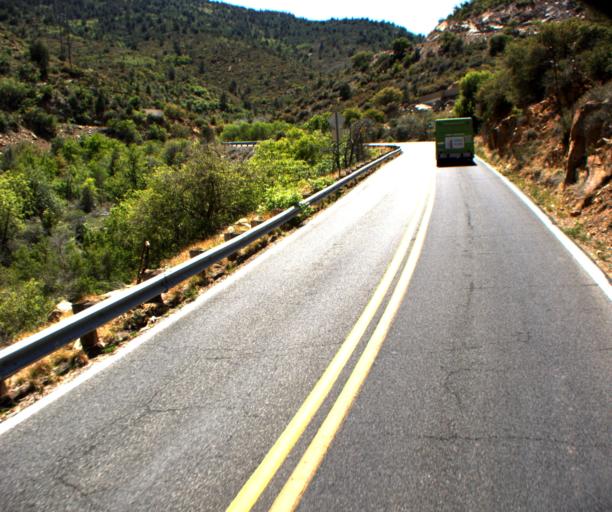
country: US
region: Arizona
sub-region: Yavapai County
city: Clarkdale
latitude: 34.7408
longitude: -112.1226
